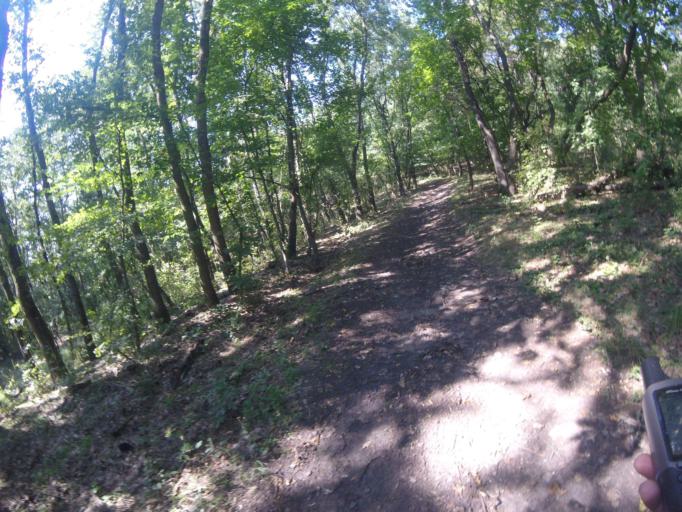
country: HU
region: Nograd
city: Bujak
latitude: 47.8969
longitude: 19.5347
